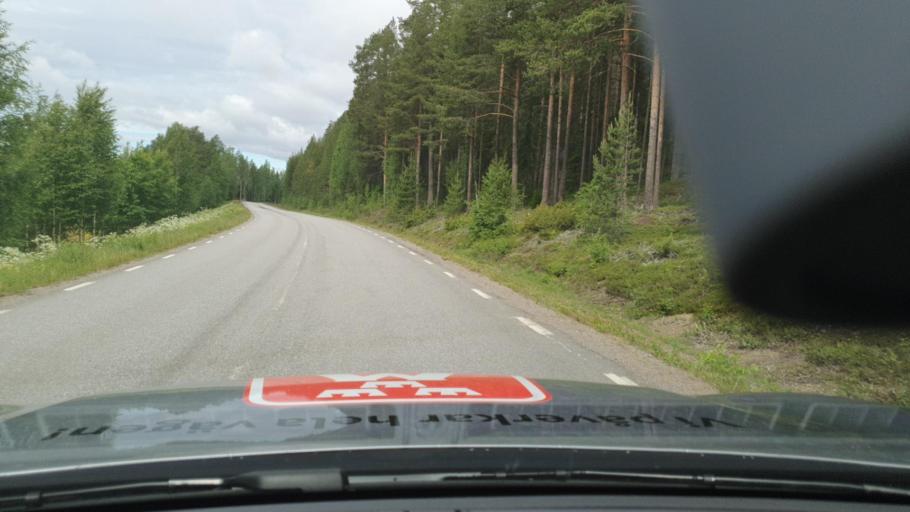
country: SE
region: Norrbotten
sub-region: Lulea Kommun
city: Ranea
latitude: 65.9877
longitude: 22.0494
